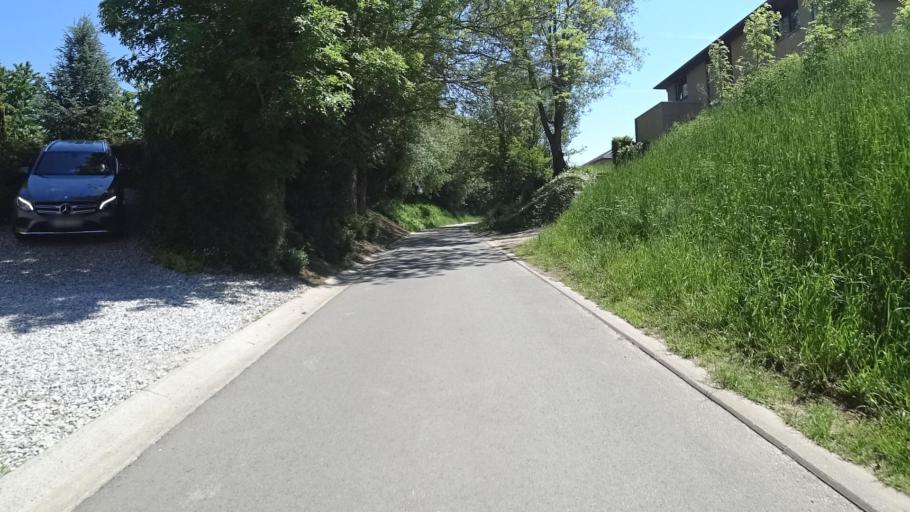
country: BE
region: Wallonia
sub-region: Province du Brabant Wallon
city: Chastre-Villeroux-Blanmont
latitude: 50.6416
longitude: 4.6511
